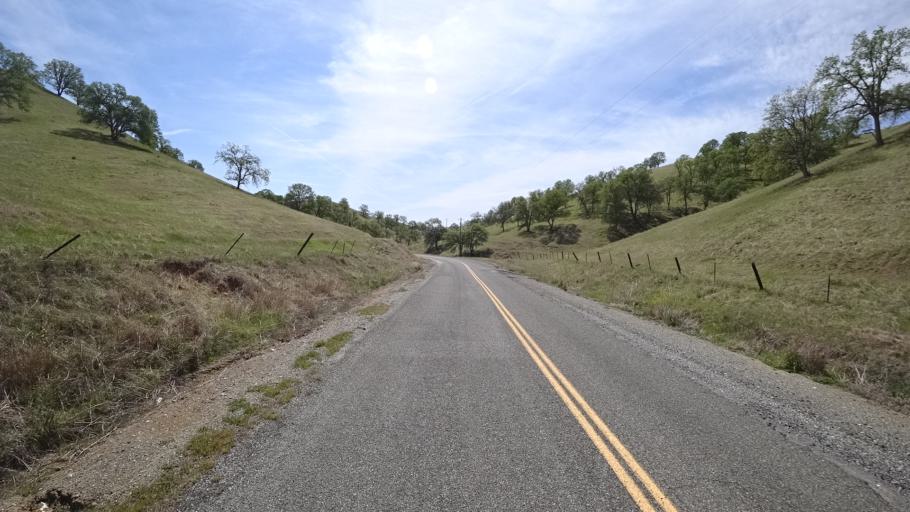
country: US
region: California
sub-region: Glenn County
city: Willows
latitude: 39.5691
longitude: -122.4427
